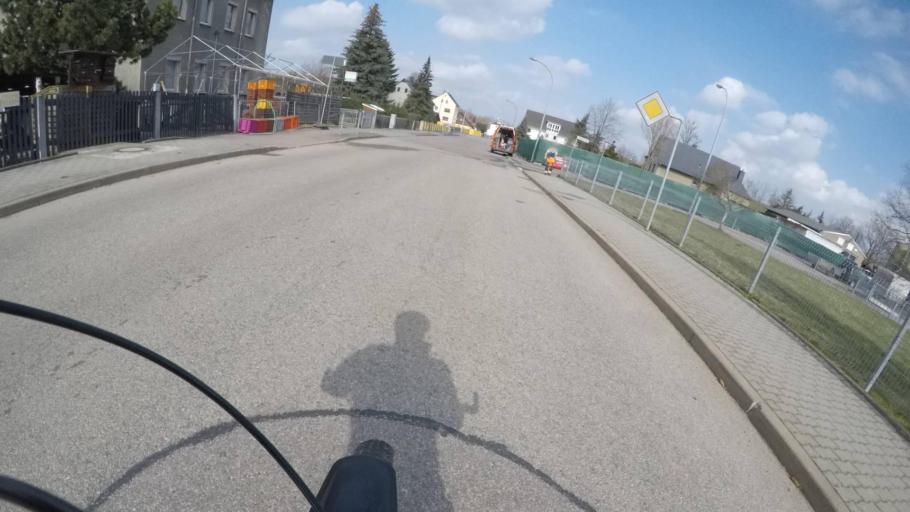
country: DE
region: Saxony
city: Limbach-Oberfrohna
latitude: 50.8658
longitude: 12.7386
